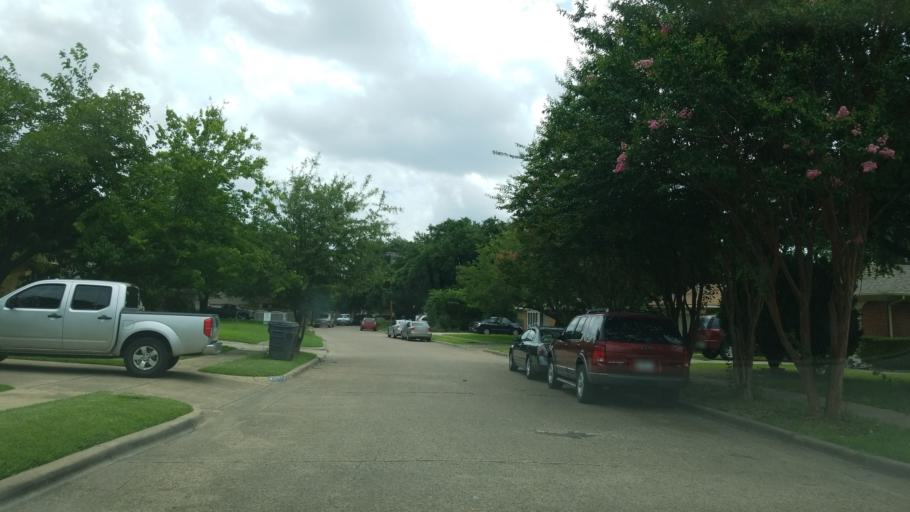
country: US
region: Texas
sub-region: Dallas County
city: Farmers Branch
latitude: 32.8887
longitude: -96.8787
